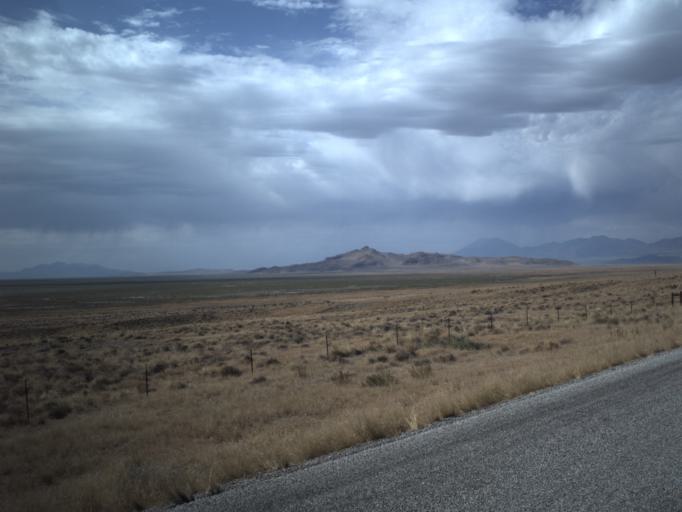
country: US
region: Utah
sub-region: Tooele County
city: Wendover
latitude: 41.4438
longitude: -113.6892
